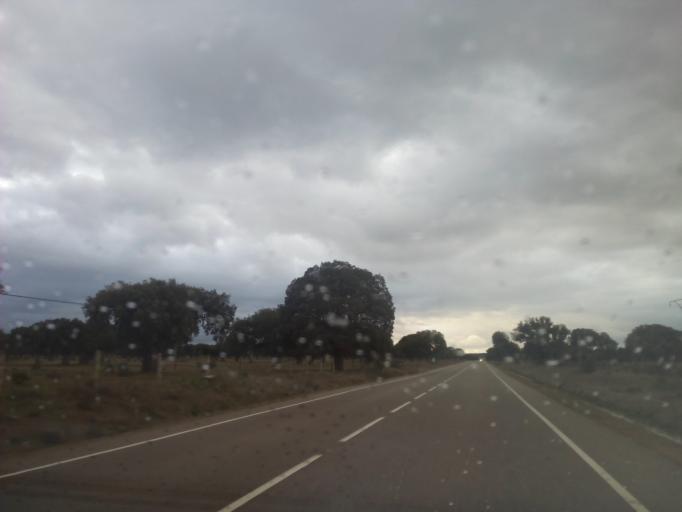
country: ES
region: Castille and Leon
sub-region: Provincia de Salamanca
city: Abusejo
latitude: 40.7247
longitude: -6.1542
